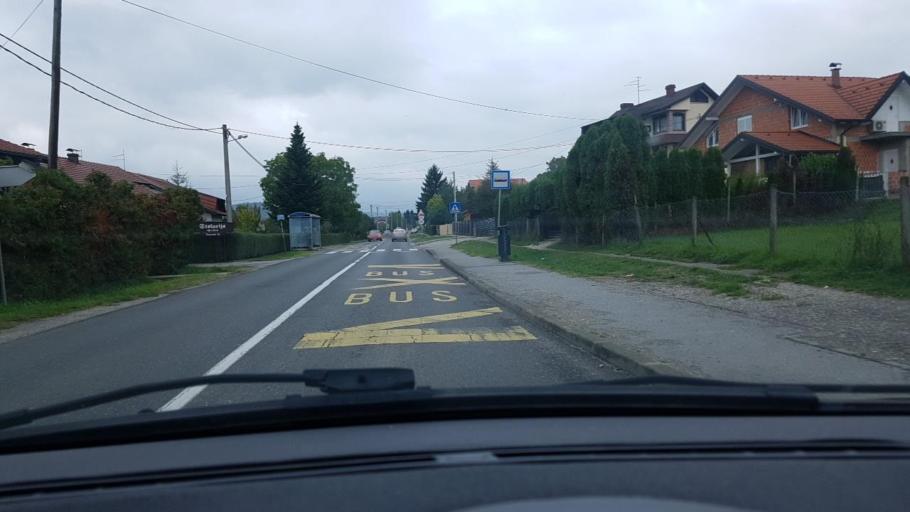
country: HR
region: Grad Zagreb
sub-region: Sesvete
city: Sesvete
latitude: 45.8625
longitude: 16.1150
